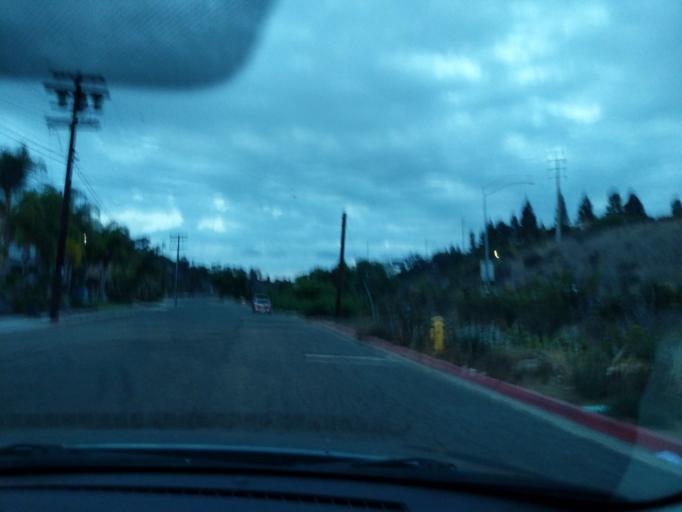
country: US
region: California
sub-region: San Diego County
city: San Diego
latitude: 32.7183
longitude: -117.1185
